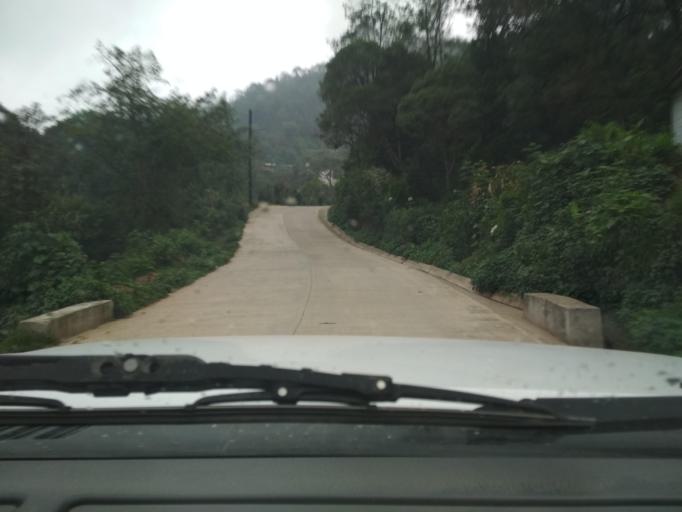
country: MX
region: Veracruz
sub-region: La Perla
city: Barrio de San Miguel
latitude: 18.9572
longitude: -97.1263
